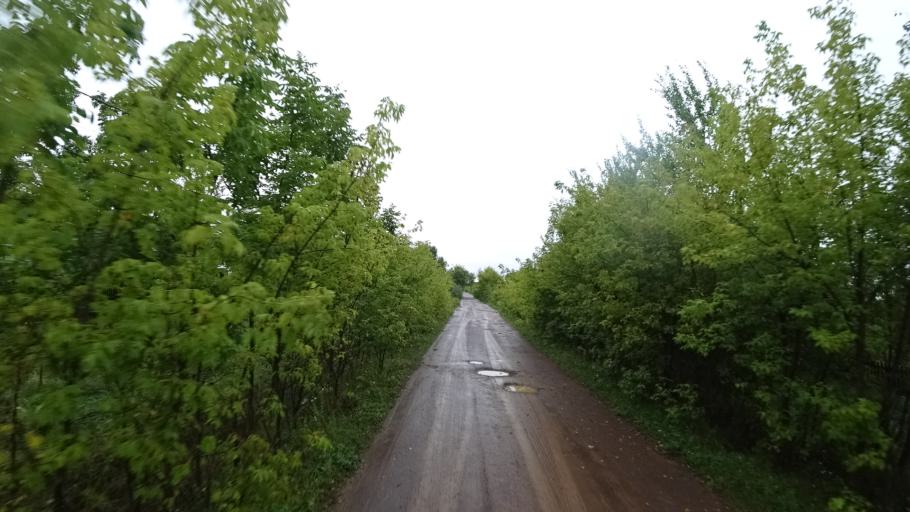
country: RU
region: Primorskiy
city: Monastyrishche
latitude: 44.2594
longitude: 132.4237
